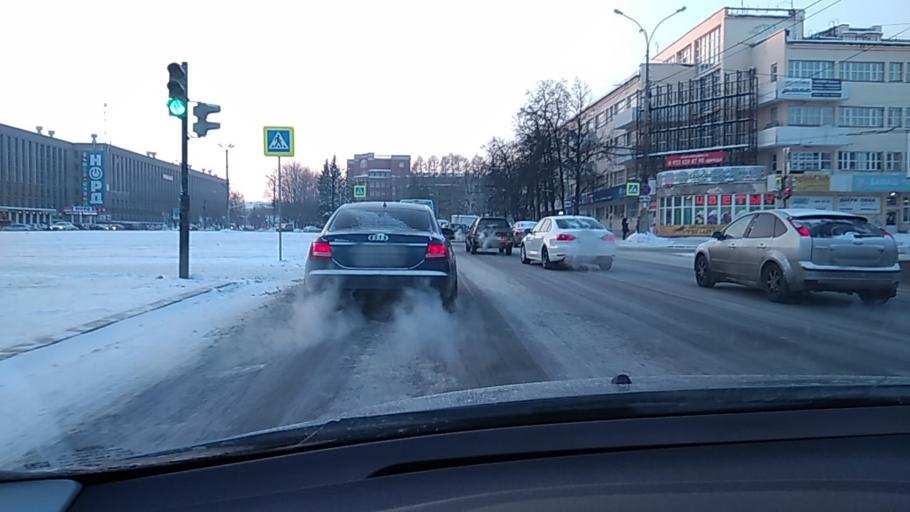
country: RU
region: Sverdlovsk
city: Yekaterinburg
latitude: 56.8864
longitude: 60.5928
